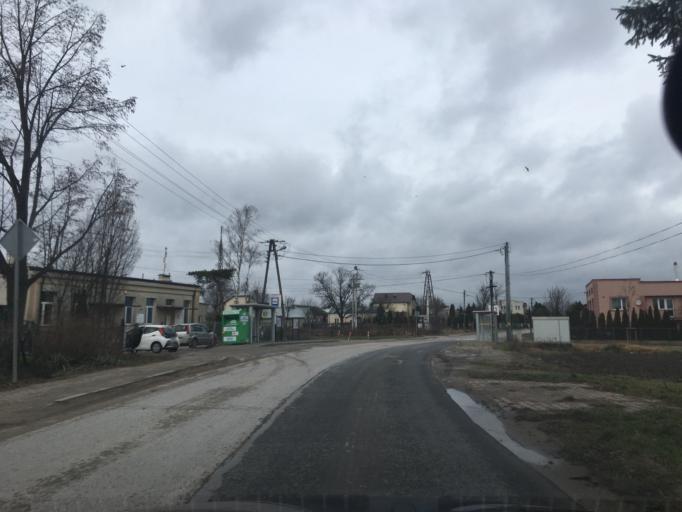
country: PL
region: Masovian Voivodeship
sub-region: Powiat piaseczynski
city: Lesznowola
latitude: 52.1101
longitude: 20.9318
